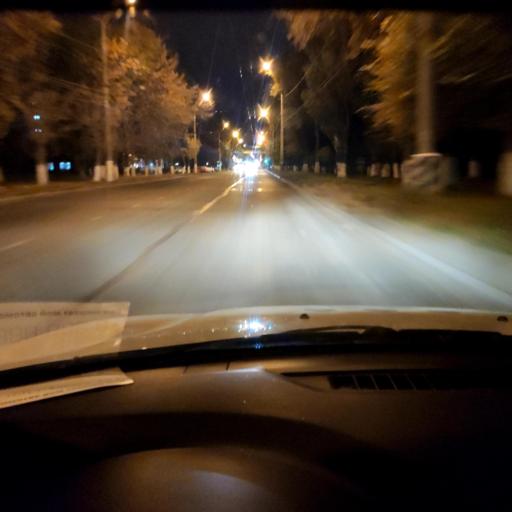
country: RU
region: Samara
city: Tol'yatti
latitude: 53.5584
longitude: 49.4531
